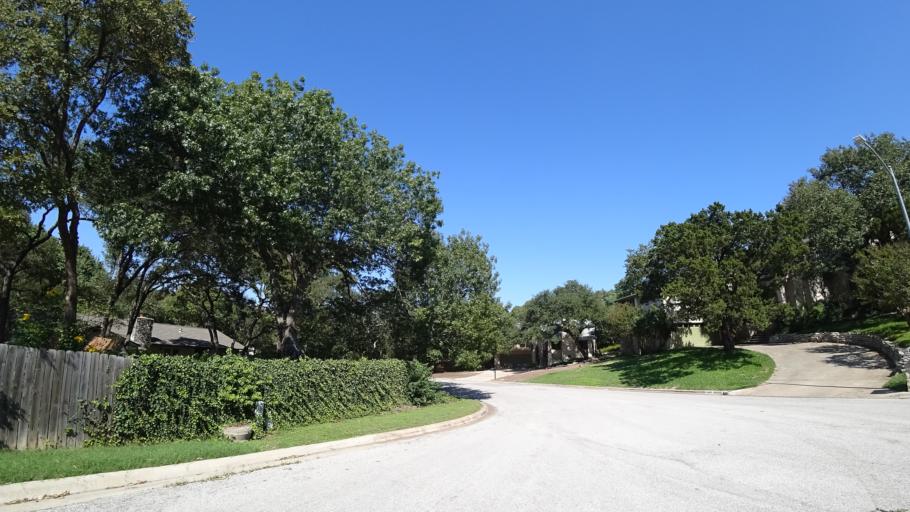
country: US
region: Texas
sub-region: Travis County
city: Rollingwood
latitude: 30.2520
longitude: -97.7944
